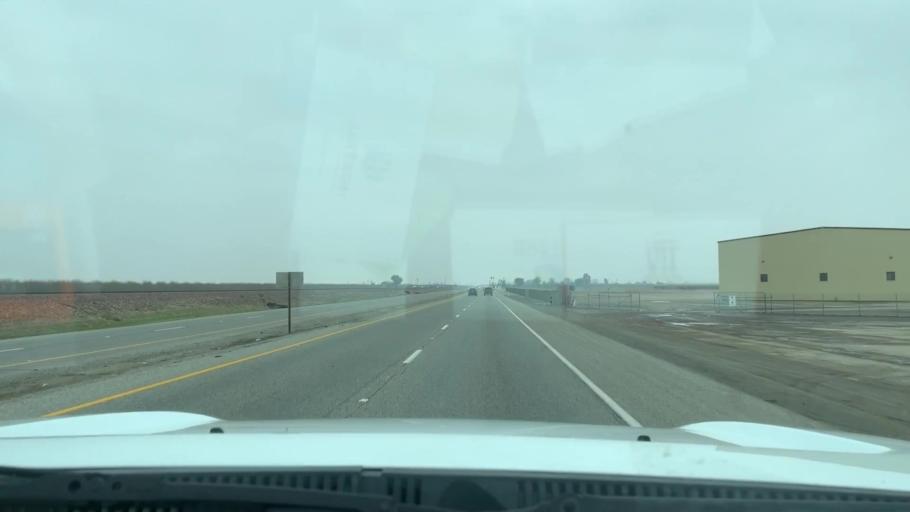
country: US
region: California
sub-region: Kern County
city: Shafter
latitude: 35.5264
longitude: -119.3030
